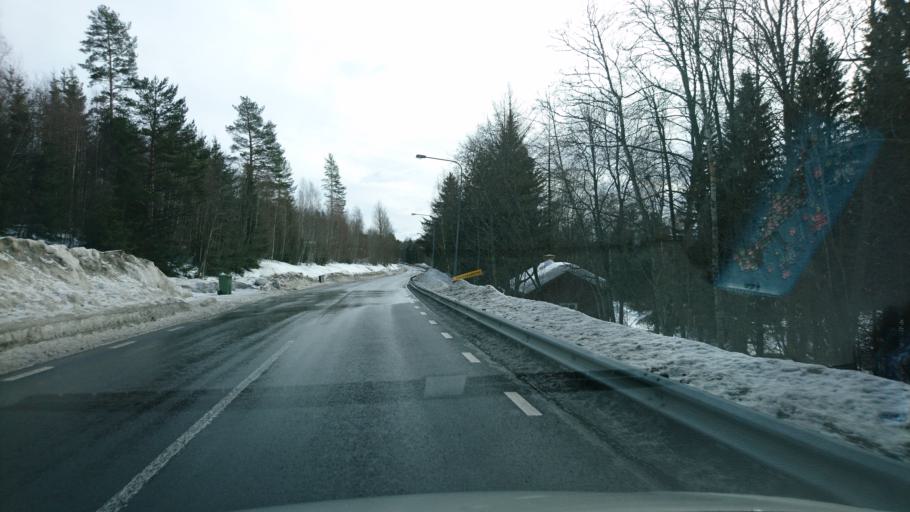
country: SE
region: Vaesternorrland
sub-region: Timra Kommun
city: Bergeforsen
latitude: 62.5868
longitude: 17.4181
